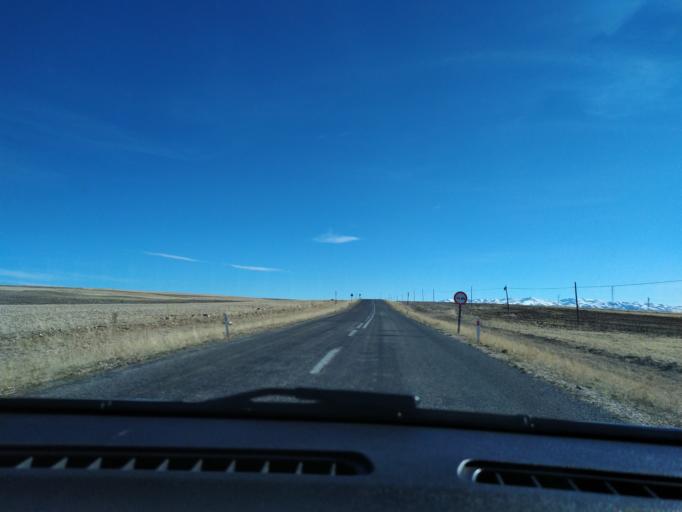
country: TR
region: Kayseri
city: Orensehir
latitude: 38.9553
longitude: 36.6865
